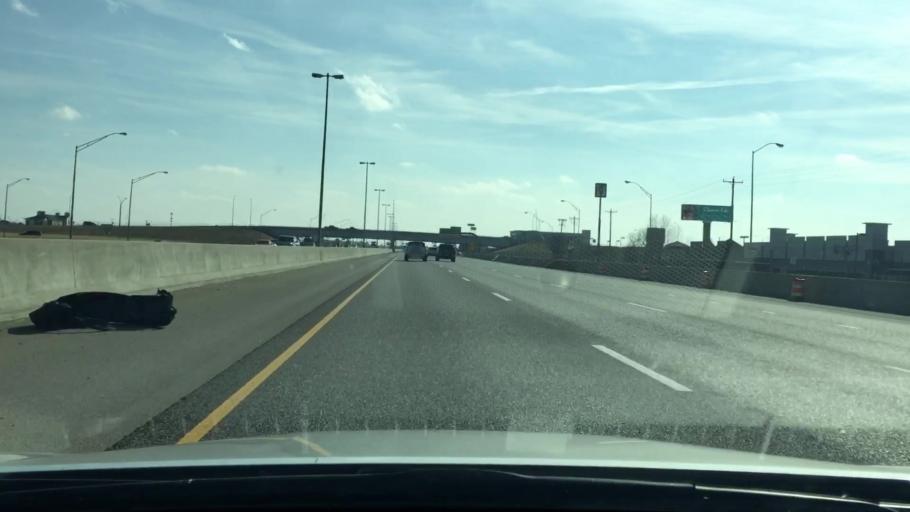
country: US
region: Oklahoma
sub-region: Cleveland County
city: Norman
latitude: 35.2361
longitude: -97.4856
